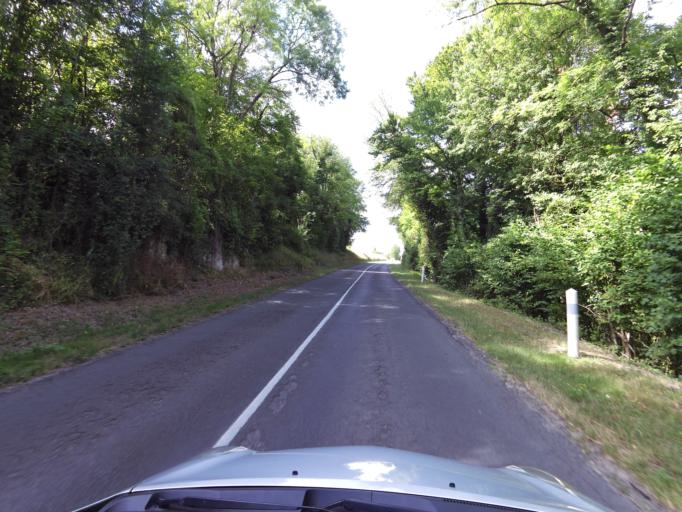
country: FR
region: Picardie
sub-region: Departement de l'Aisne
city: Bruyeres-et-Montberault
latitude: 49.4806
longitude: 3.6677
